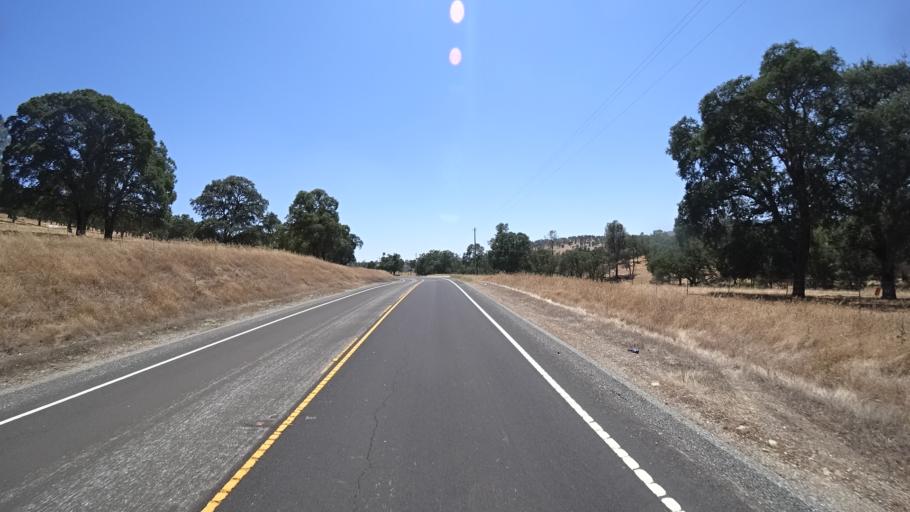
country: US
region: California
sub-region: Calaveras County
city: Angels Camp
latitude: 38.0426
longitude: -120.5324
